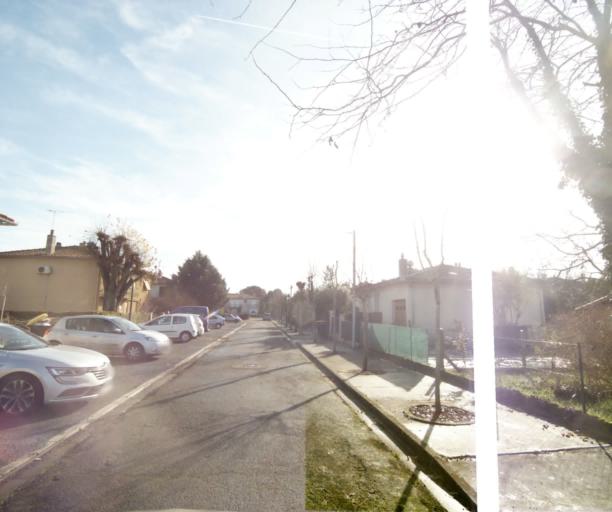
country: FR
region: Midi-Pyrenees
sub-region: Departement de la Haute-Garonne
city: Villemur-sur-Tarn
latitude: 43.8640
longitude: 1.4937
